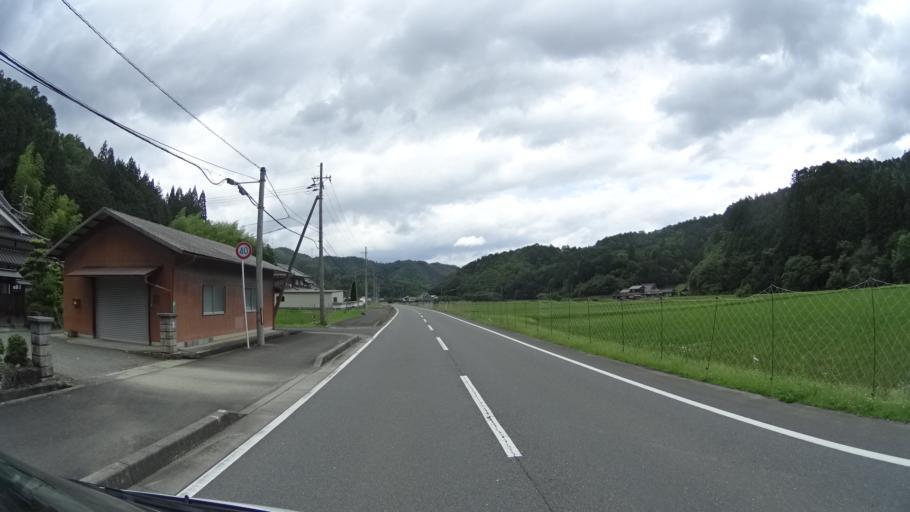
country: JP
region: Kyoto
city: Kameoka
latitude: 35.0856
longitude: 135.4177
